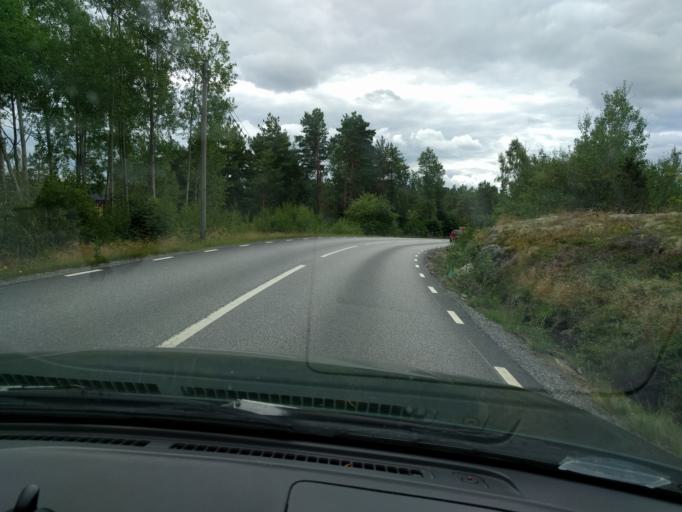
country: SE
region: Soedermanland
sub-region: Nykopings Kommun
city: Svalsta
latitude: 58.5095
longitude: 16.8507
